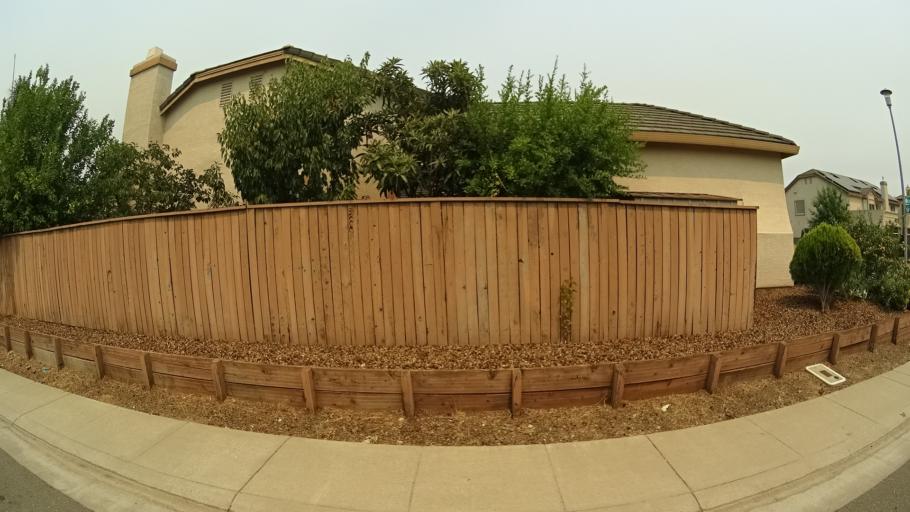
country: US
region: California
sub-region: Sacramento County
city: Laguna
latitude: 38.4018
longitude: -121.4241
